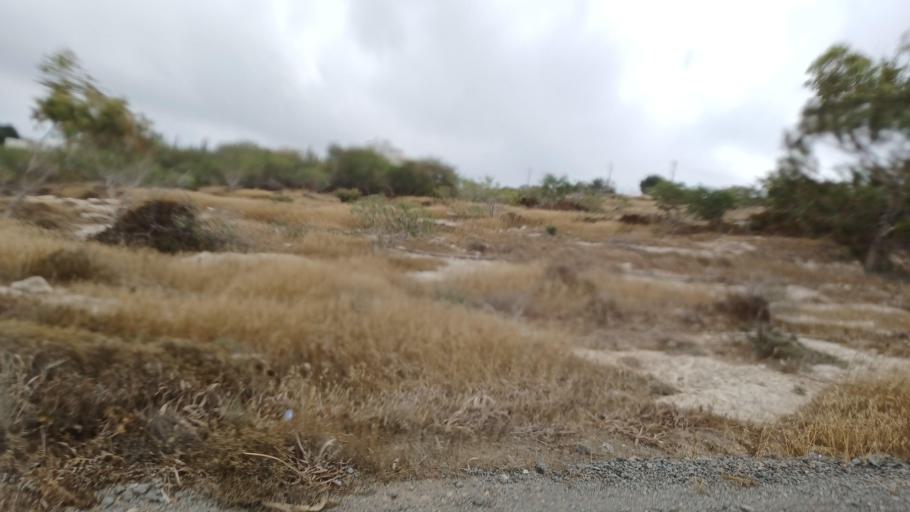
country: CY
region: Ammochostos
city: Protaras
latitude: 35.0058
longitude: 34.0272
